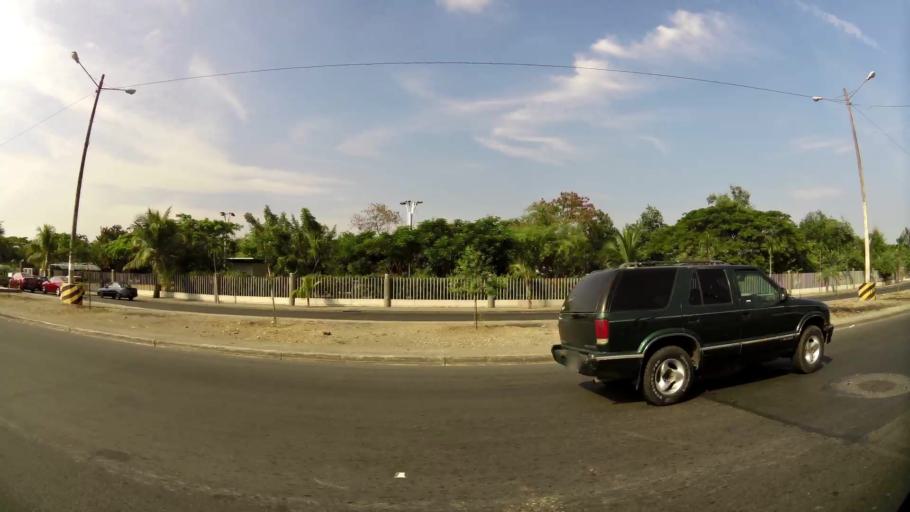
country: EC
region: Guayas
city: Guayaquil
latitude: -2.1879
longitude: -79.9063
